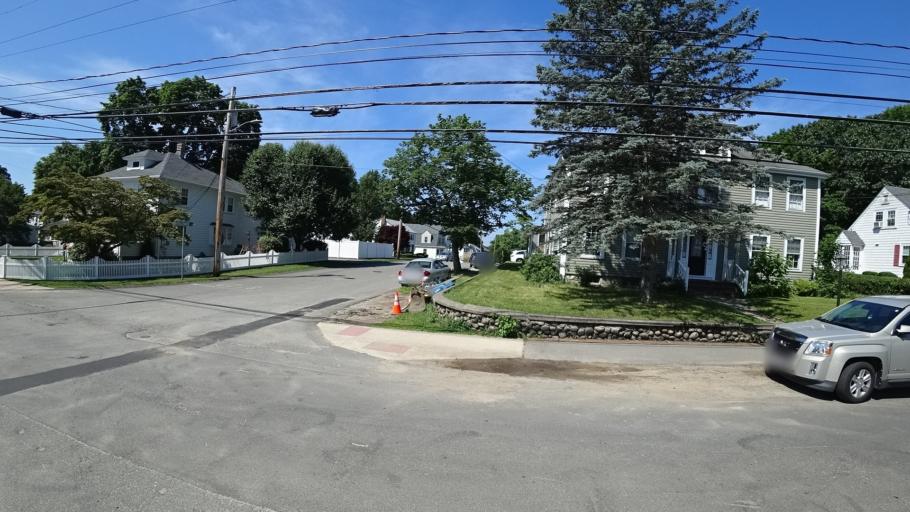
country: US
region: Massachusetts
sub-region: Norfolk County
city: Dedham
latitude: 42.2383
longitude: -71.1596
